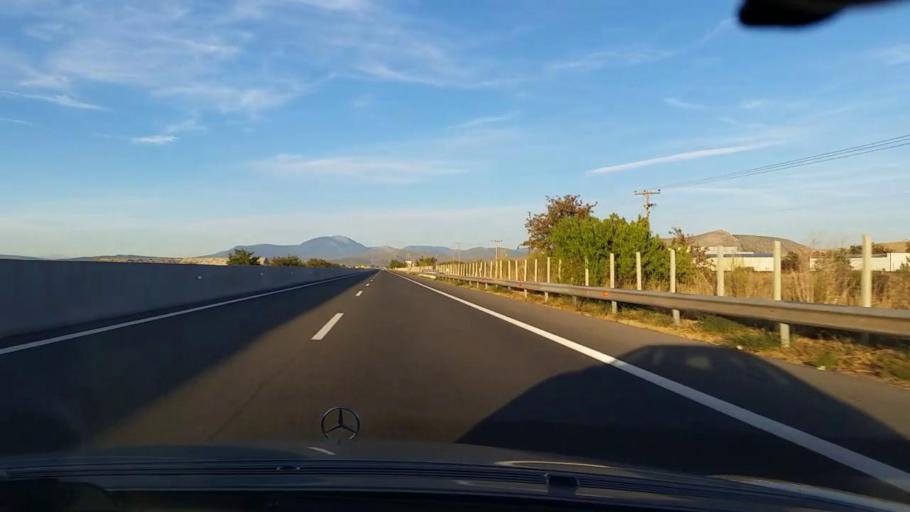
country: GR
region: Central Greece
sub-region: Nomos Voiotias
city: Thivai
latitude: 38.3698
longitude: 23.3751
